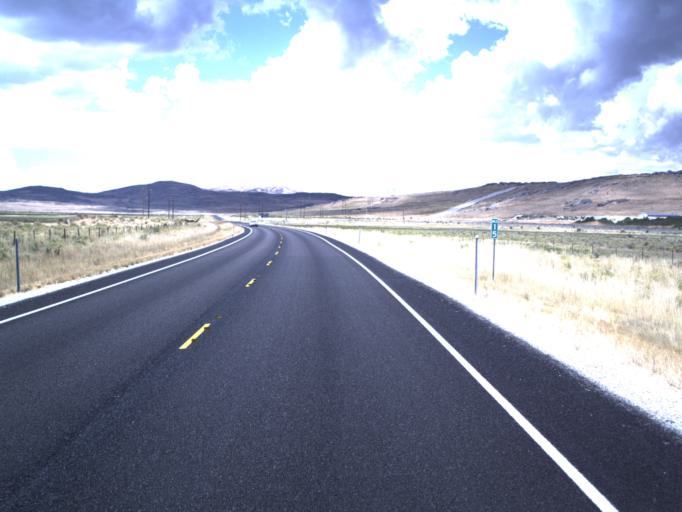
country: US
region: Utah
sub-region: Box Elder County
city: Tremonton
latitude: 41.6268
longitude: -112.3984
